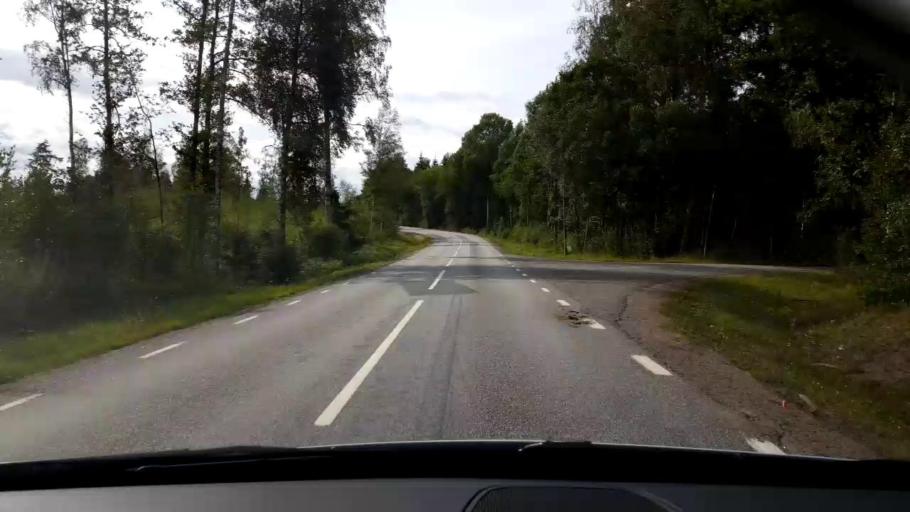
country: SE
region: Joenkoeping
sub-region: Vetlanda Kommun
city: Vetlanda
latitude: 57.3800
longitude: 15.0327
